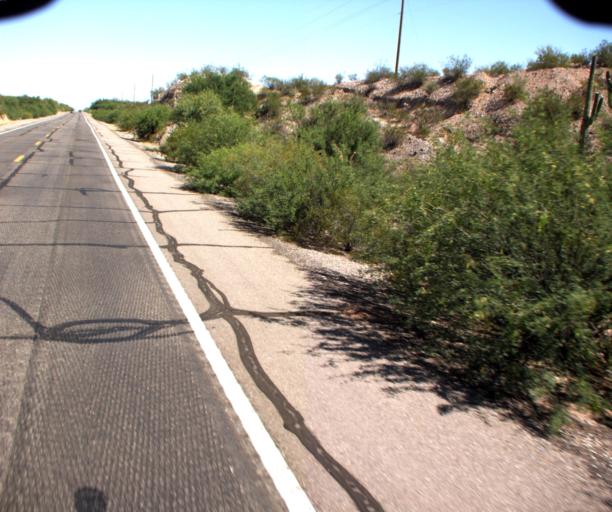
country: US
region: Arizona
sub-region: Pinal County
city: Mammoth
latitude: 32.7808
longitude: -110.6659
